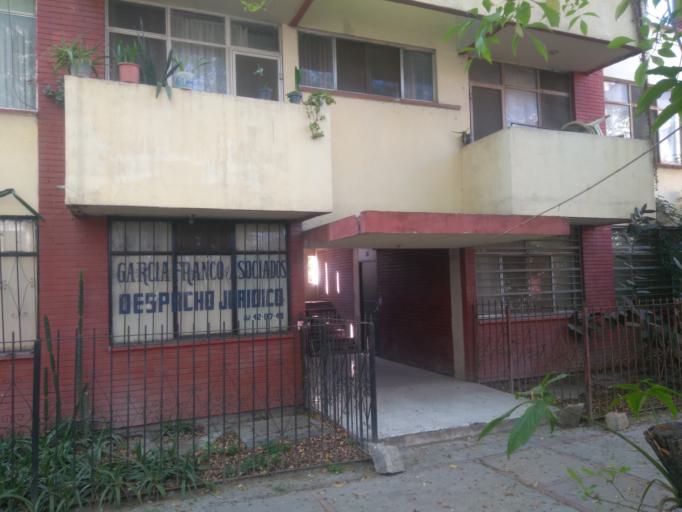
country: MX
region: Nuevo Leon
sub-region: Monterrey
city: Monterrey
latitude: 25.6680
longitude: -100.3019
